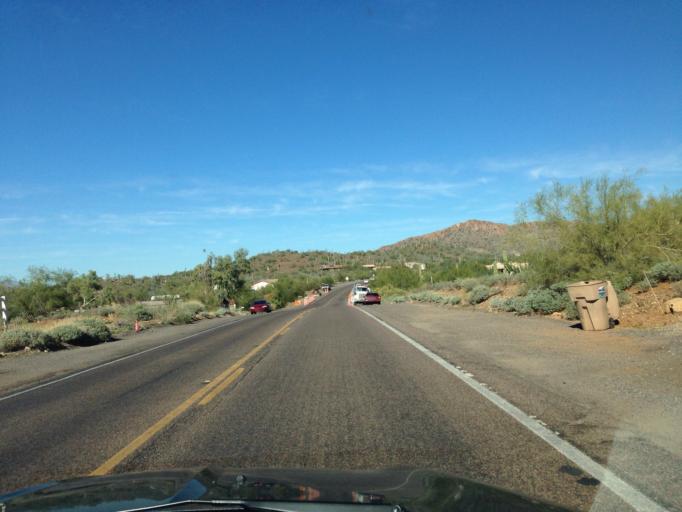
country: US
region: Arizona
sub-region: Maricopa County
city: Anthem
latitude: 33.8510
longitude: -112.0627
